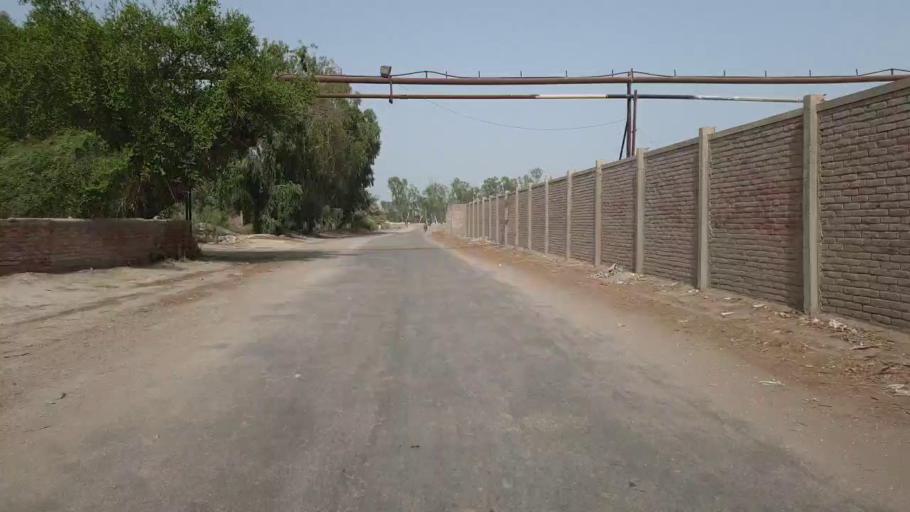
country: PK
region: Sindh
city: Daulatpur
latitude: 26.5590
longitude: 67.9860
